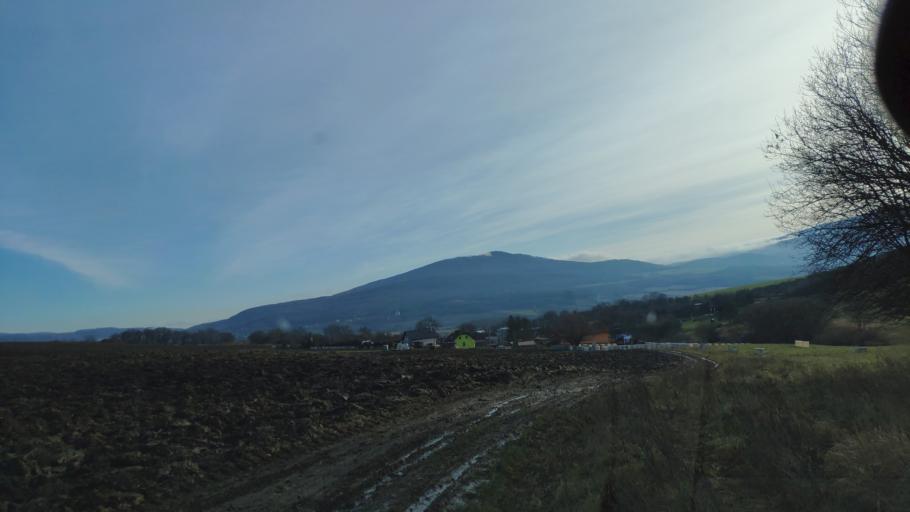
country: SK
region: Kosicky
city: Kosice
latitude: 48.6877
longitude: 21.3917
